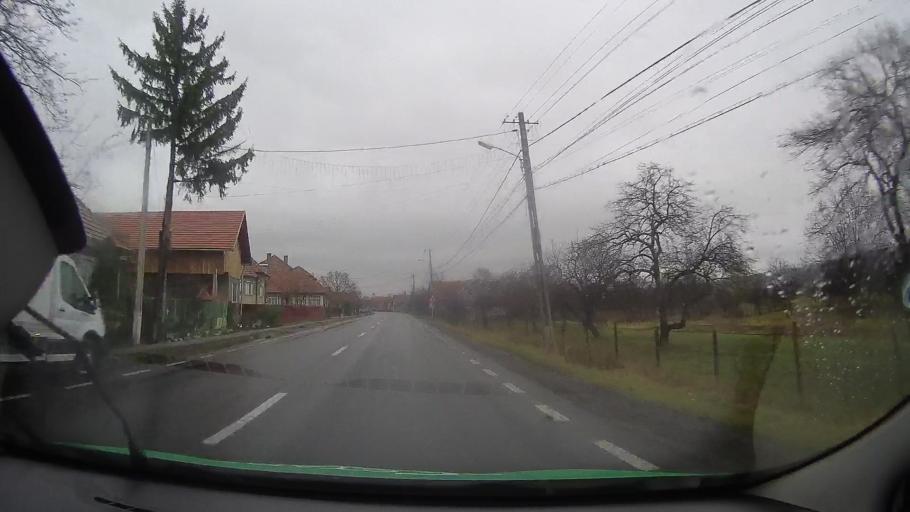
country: RO
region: Mures
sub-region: Comuna Brancovenesti
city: Valenii de Mures
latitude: 46.8879
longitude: 24.7931
